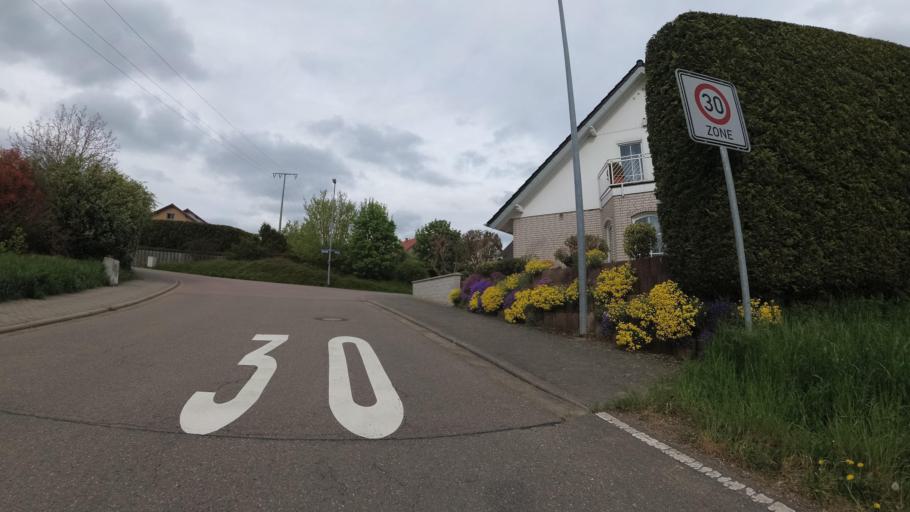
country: DE
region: Rheinland-Pfalz
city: Zweibrucken
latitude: 49.2356
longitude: 7.3454
